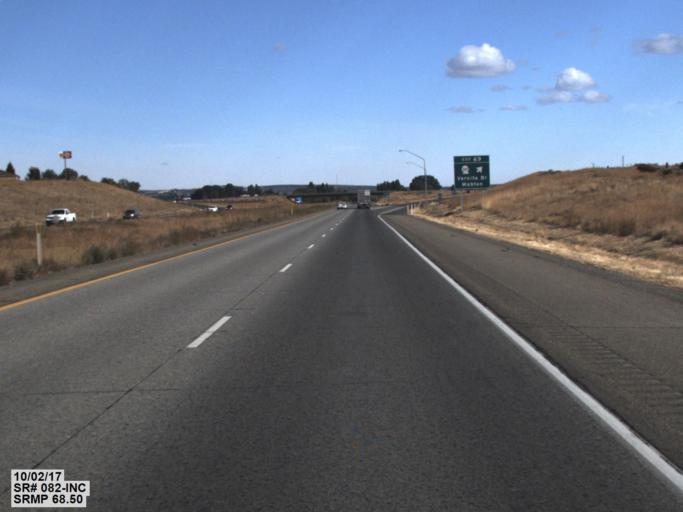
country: US
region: Washington
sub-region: Yakima County
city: Sunnyside
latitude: 46.3060
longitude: -119.9878
